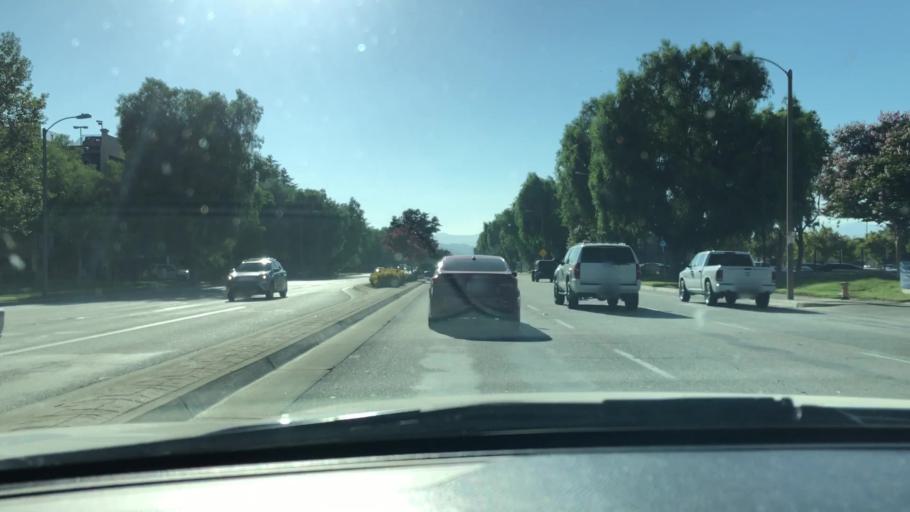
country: US
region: California
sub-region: Los Angeles County
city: Santa Clarita
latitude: 34.4185
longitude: -118.5585
